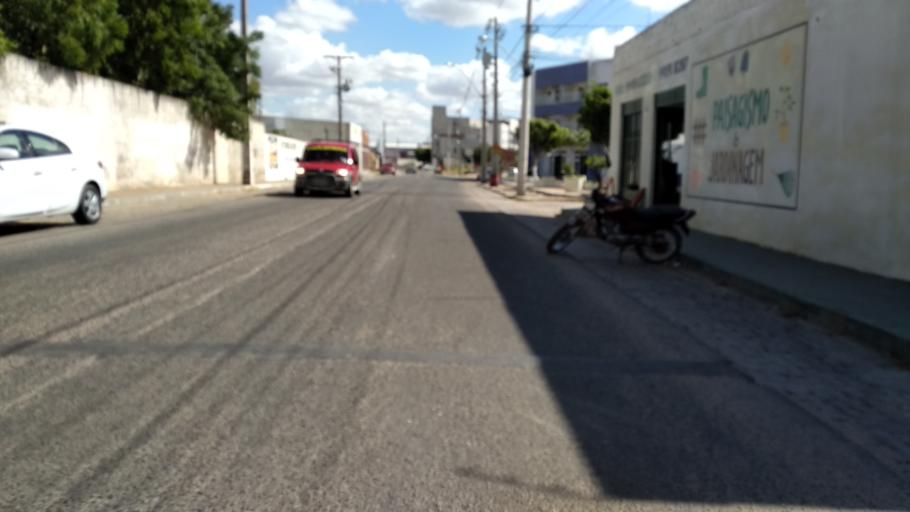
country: BR
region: Bahia
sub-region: Guanambi
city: Guanambi
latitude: -14.2334
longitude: -42.7791
